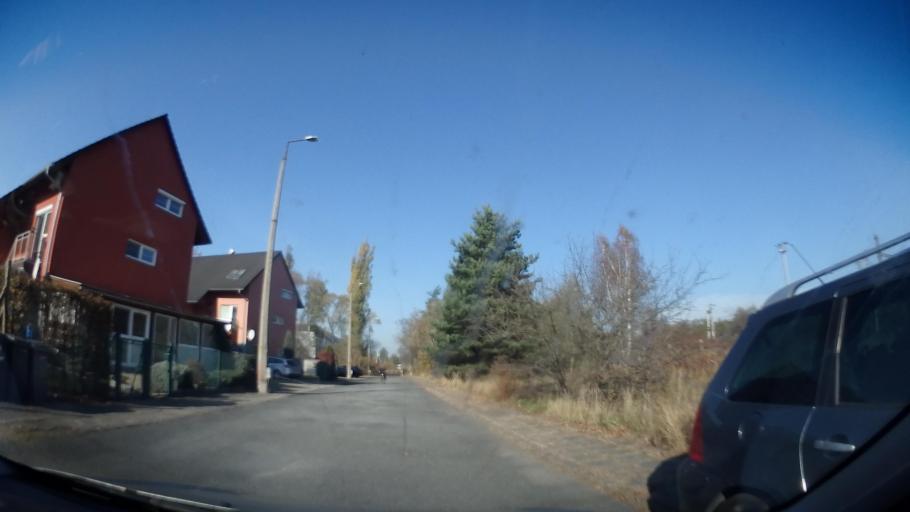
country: CZ
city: Tyniste nad Orlici
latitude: 50.1591
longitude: 16.0676
